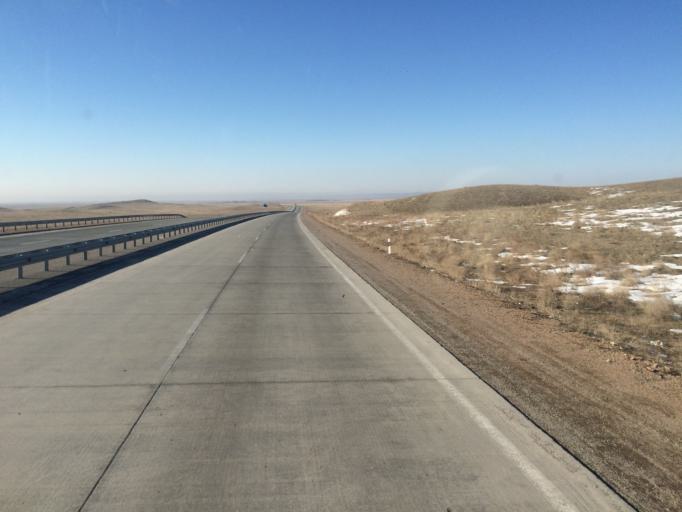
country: KZ
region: Zhambyl
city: Georgiyevka
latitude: 43.3392
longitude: 74.4626
